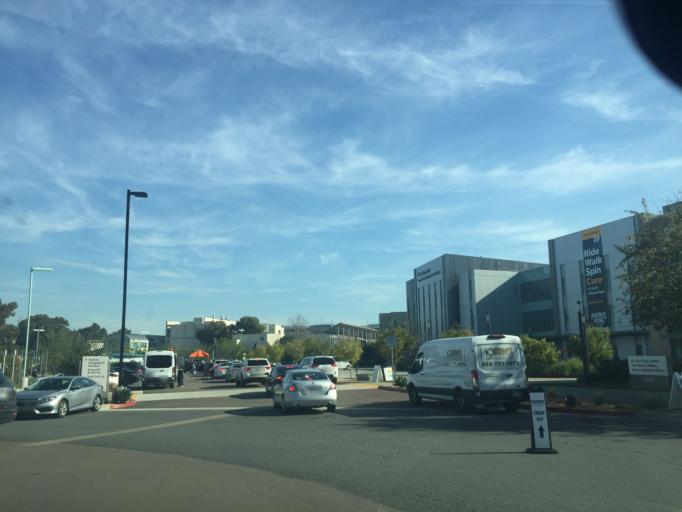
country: US
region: California
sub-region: San Diego County
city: La Jolla
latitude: 32.8785
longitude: -117.2251
